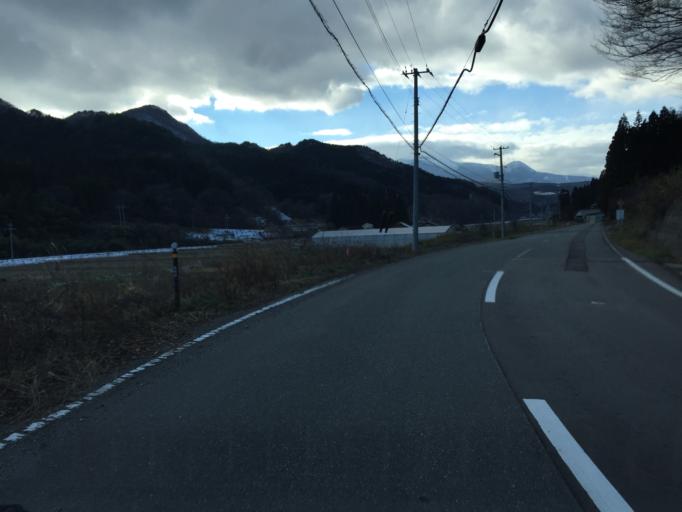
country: JP
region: Fukushima
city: Nihommatsu
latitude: 37.6720
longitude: 140.4028
